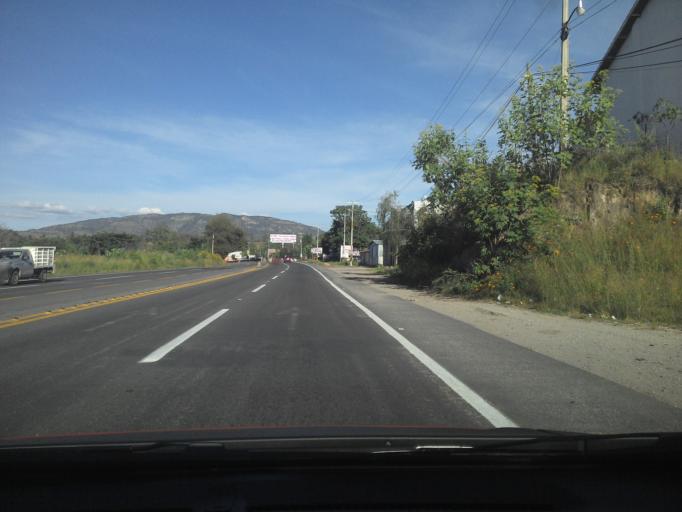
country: MX
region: Jalisco
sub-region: Tala
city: Los Ruisenores
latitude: 20.7202
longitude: -103.6268
